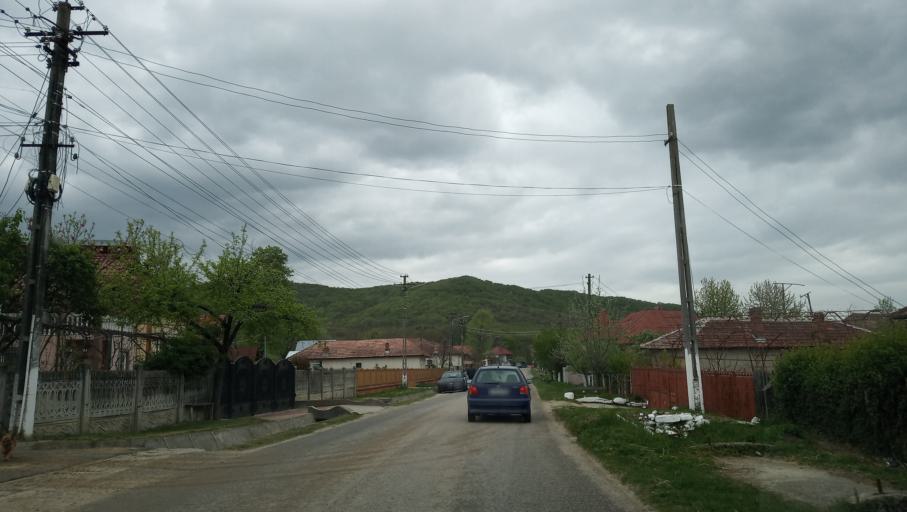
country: RO
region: Valcea
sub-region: Municipiul Ramnicu Valcea
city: Goranu
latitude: 45.1502
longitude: 24.3949
